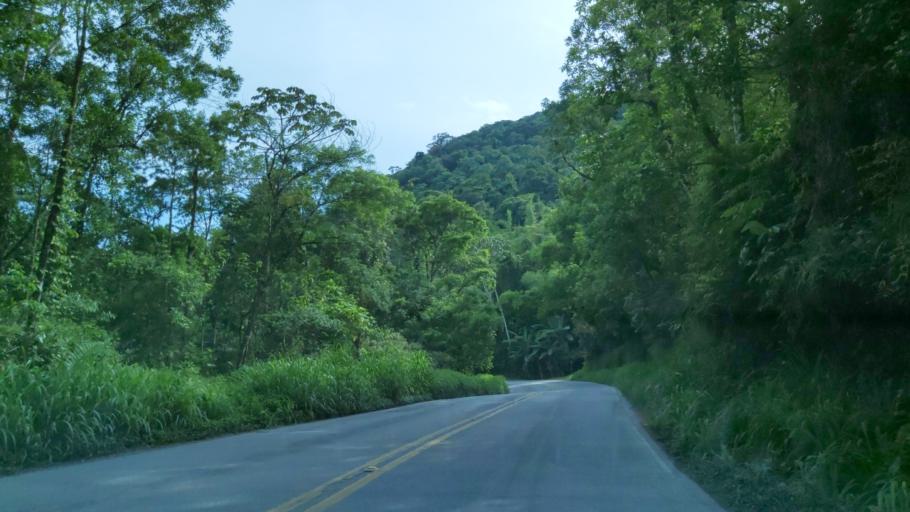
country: BR
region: Sao Paulo
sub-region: Miracatu
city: Miracatu
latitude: -24.0406
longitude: -47.5678
